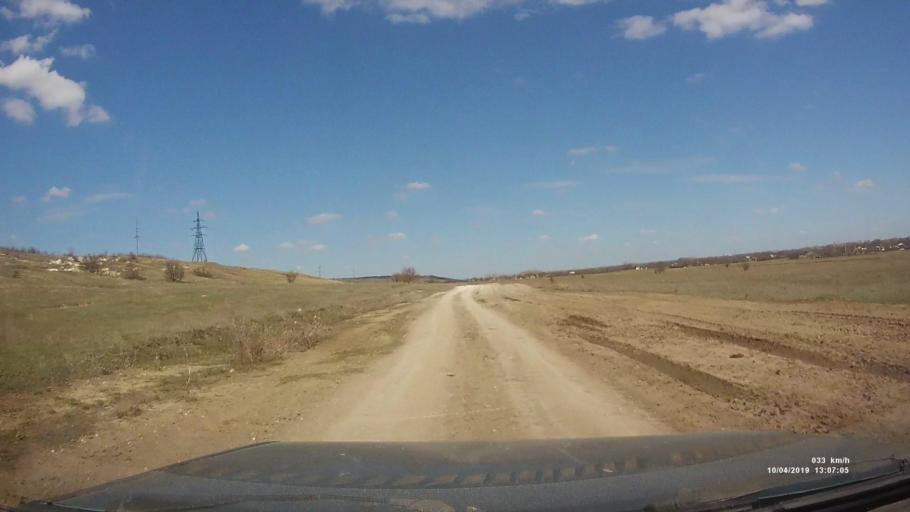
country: RU
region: Rostov
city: Masalovka
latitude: 48.3941
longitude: 40.2388
